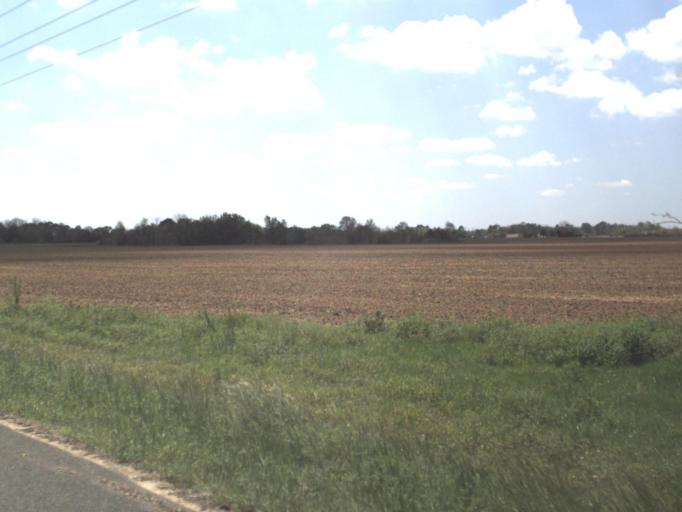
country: US
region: Florida
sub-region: Okaloosa County
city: Crestview
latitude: 30.8236
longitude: -86.6760
